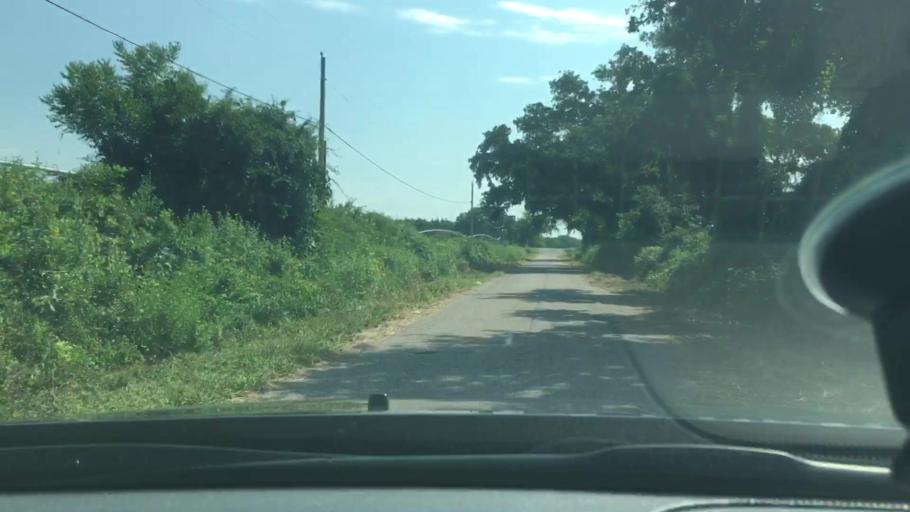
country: US
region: Oklahoma
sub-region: Bryan County
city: Colbert
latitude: 33.8965
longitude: -96.5521
